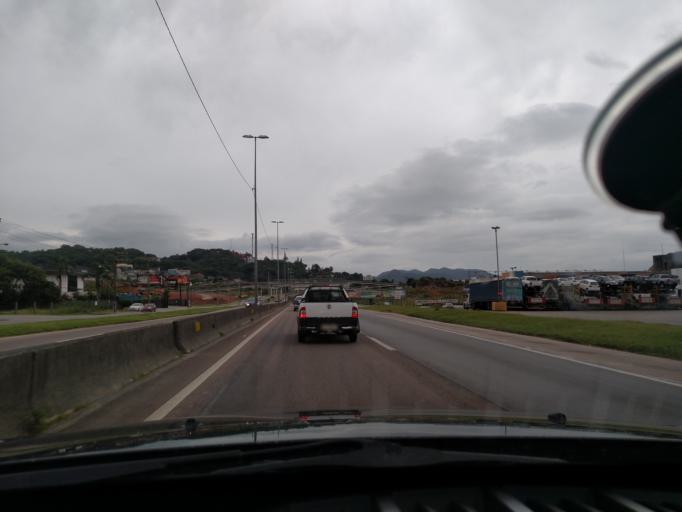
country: BR
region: Santa Catarina
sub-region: Biguacu
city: Biguacu
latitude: -27.5266
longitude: -48.6350
